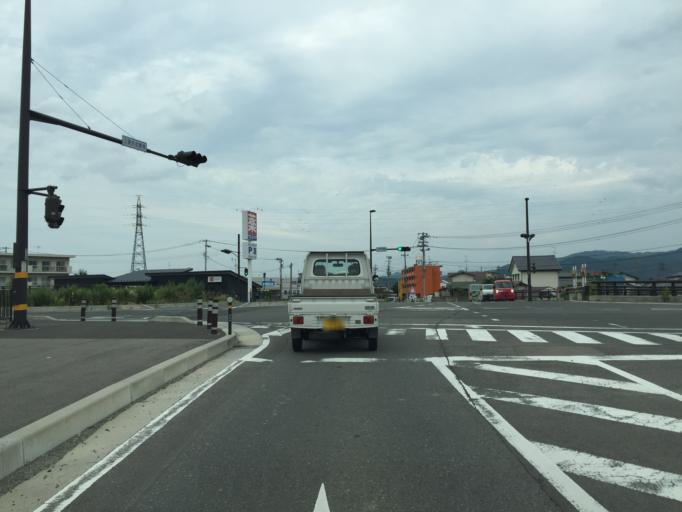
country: JP
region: Fukushima
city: Fukushima-shi
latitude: 37.7310
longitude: 140.4420
